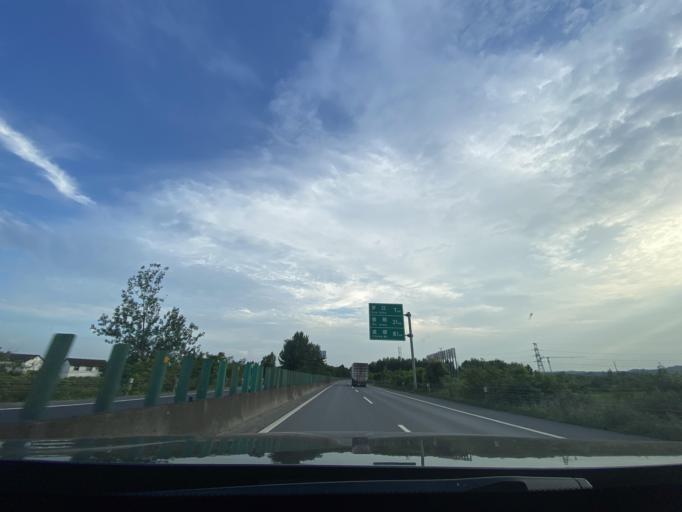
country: CN
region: Sichuan
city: Luojiang
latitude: 31.3727
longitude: 104.5448
